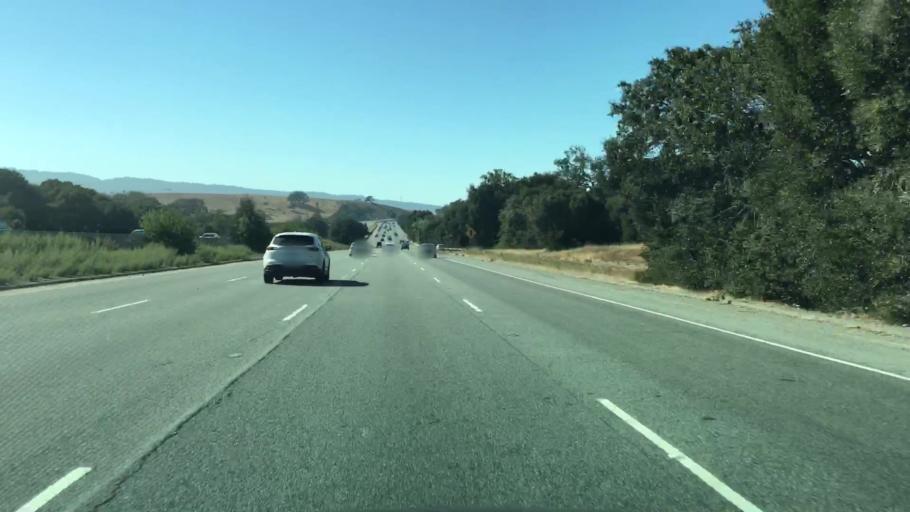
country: US
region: California
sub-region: San Mateo County
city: Ladera
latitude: 37.4076
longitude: -122.1971
